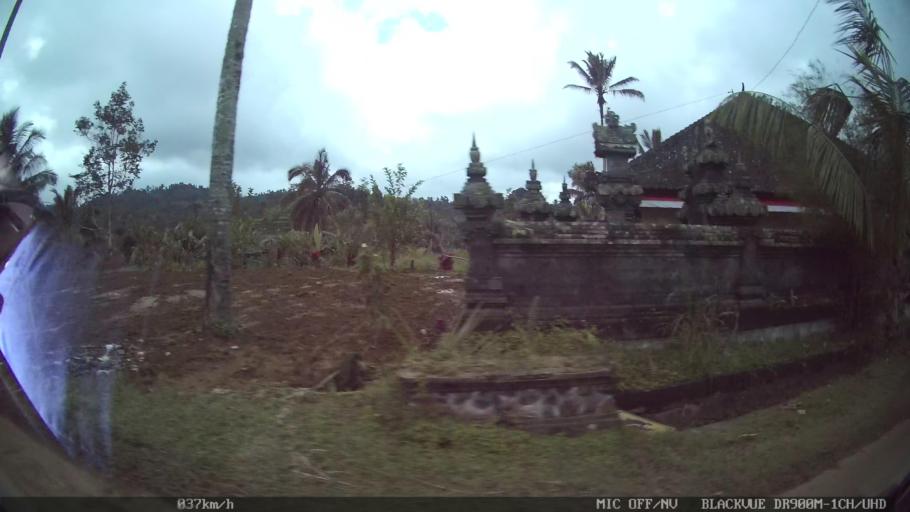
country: ID
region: Bali
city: Peneng
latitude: -8.3572
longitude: 115.2127
